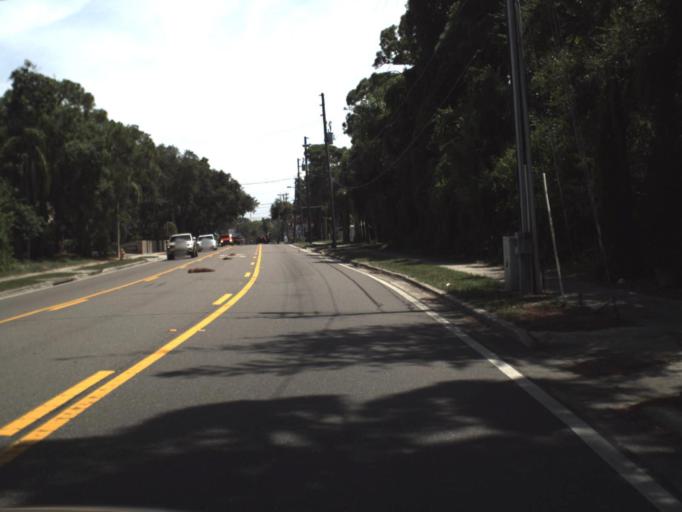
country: US
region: Florida
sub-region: Pinellas County
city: Dunedin
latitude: 28.0259
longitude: -82.7900
